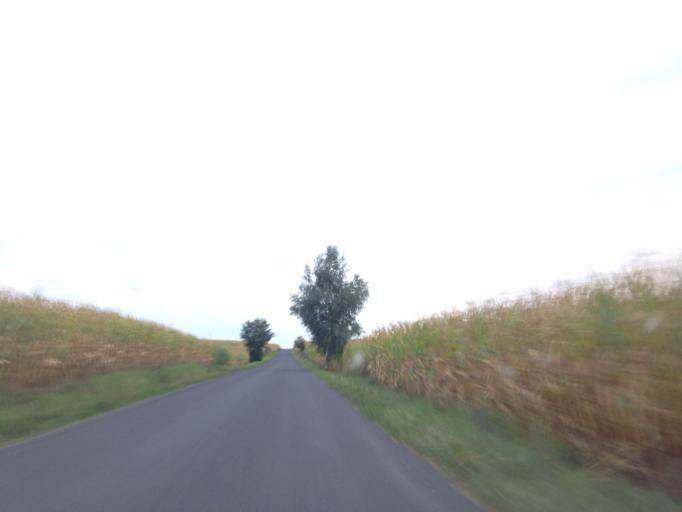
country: PL
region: Kujawsko-Pomorskie
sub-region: Powiat brodnicki
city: Brzozie
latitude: 53.3164
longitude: 19.6734
